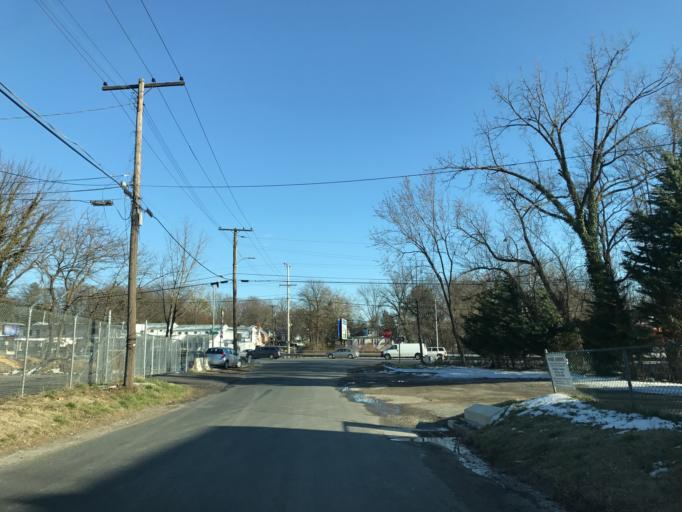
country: US
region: Maryland
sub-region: Baltimore County
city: Rosedale
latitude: 39.3175
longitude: -76.5166
